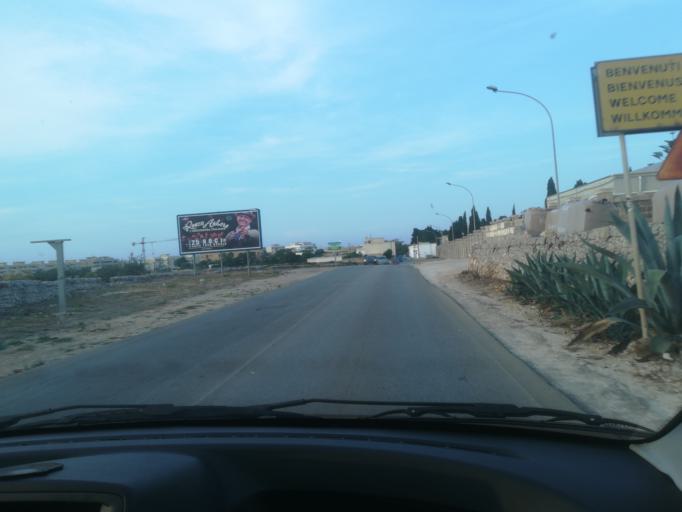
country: IT
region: Apulia
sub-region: Provincia di Bari
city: Monopoli
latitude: 40.9412
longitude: 17.2967
